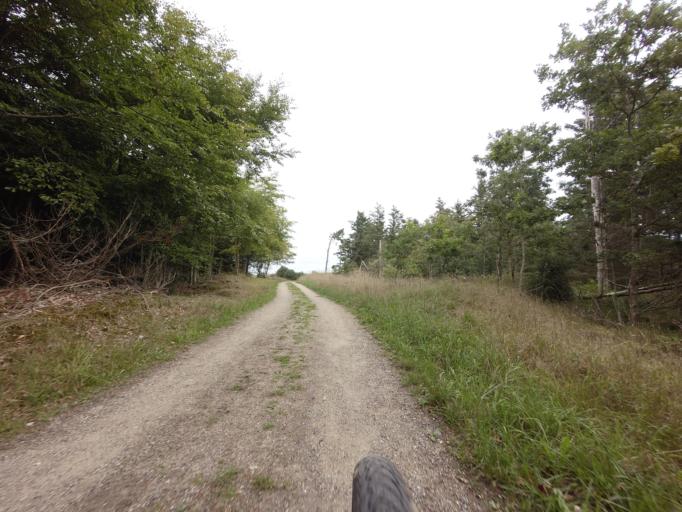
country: DK
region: North Denmark
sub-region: Hjorring Kommune
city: Hirtshals
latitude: 57.5515
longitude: 9.9205
